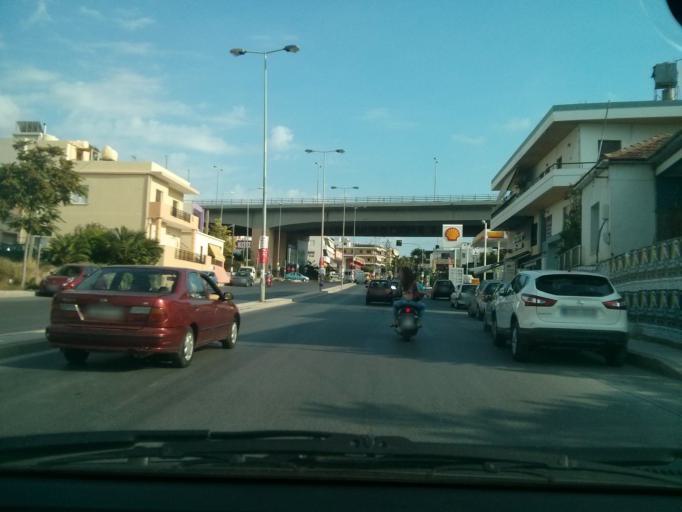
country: GR
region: Crete
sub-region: Nomos Irakleiou
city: Irakleion
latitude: 35.3216
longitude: 25.1429
